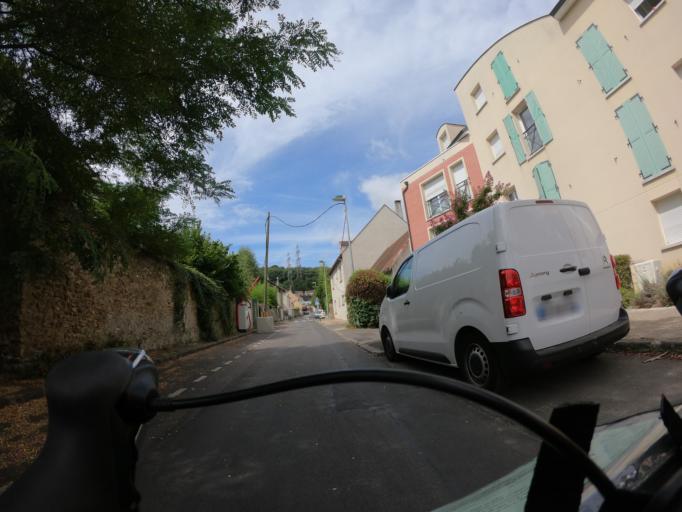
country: FR
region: Ile-de-France
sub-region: Departement de l'Essonne
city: Igny
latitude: 48.7432
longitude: 2.2279
